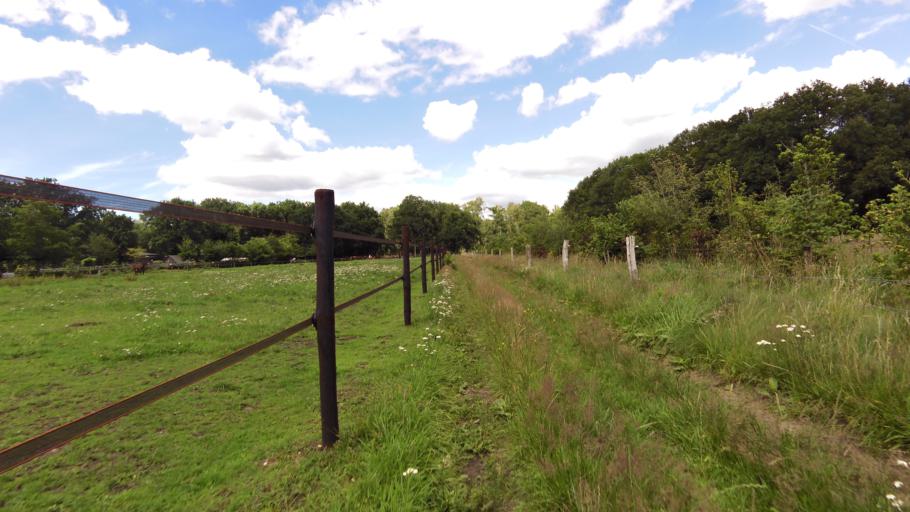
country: NL
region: Gelderland
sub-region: Gemeente Epe
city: Vaassen
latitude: 52.2594
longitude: 5.9331
